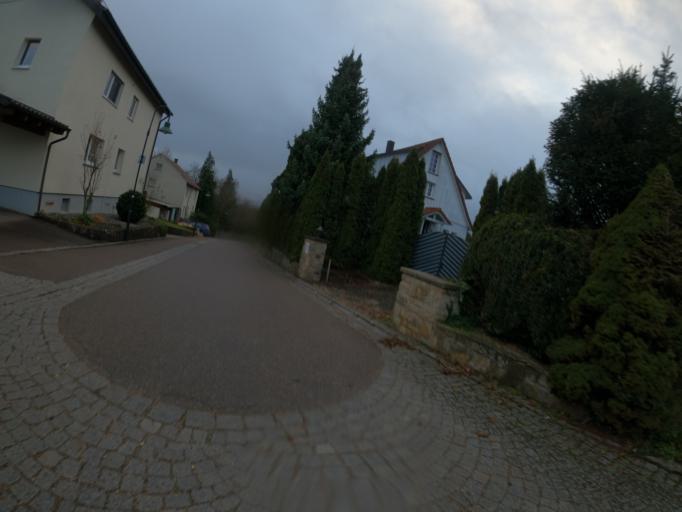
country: DE
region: Baden-Wuerttemberg
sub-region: Regierungsbezirk Stuttgart
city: Waschenbeuren
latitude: 48.7630
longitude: 9.6857
